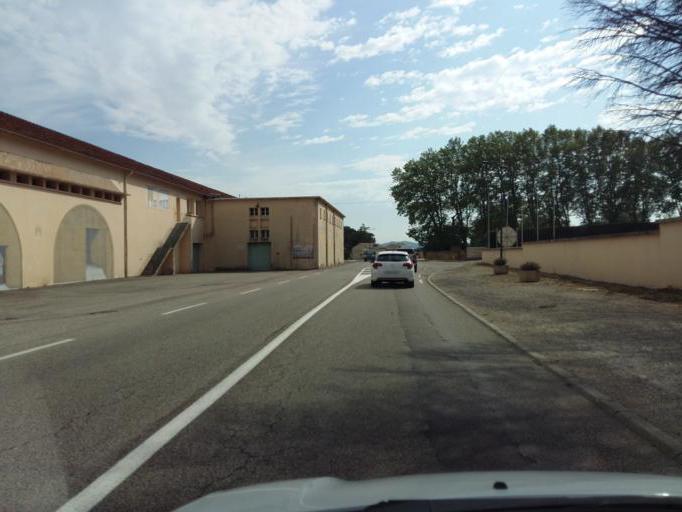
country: FR
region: Rhone-Alpes
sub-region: Departement de la Drome
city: Suze-la-Rousse
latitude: 44.2868
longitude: 4.8370
